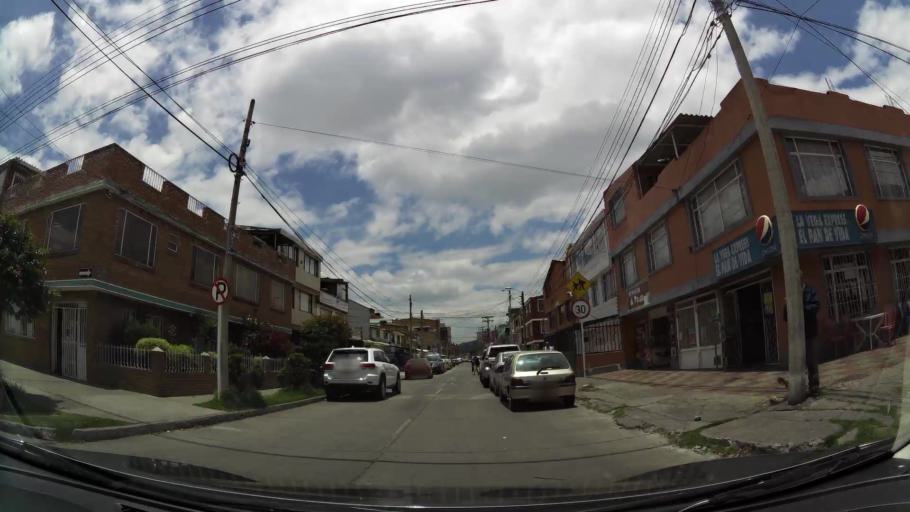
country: CO
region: Bogota D.C.
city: Barrio San Luis
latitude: 4.7135
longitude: -74.0573
